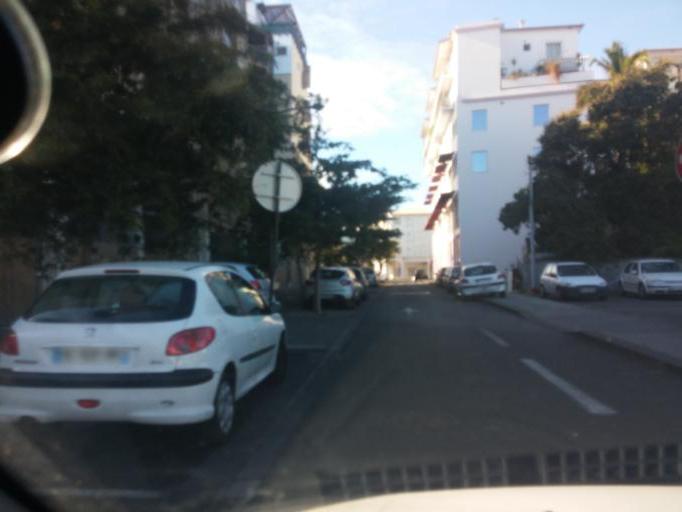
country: RE
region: Reunion
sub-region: Reunion
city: Le Port
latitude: -20.9384
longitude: 55.2954
